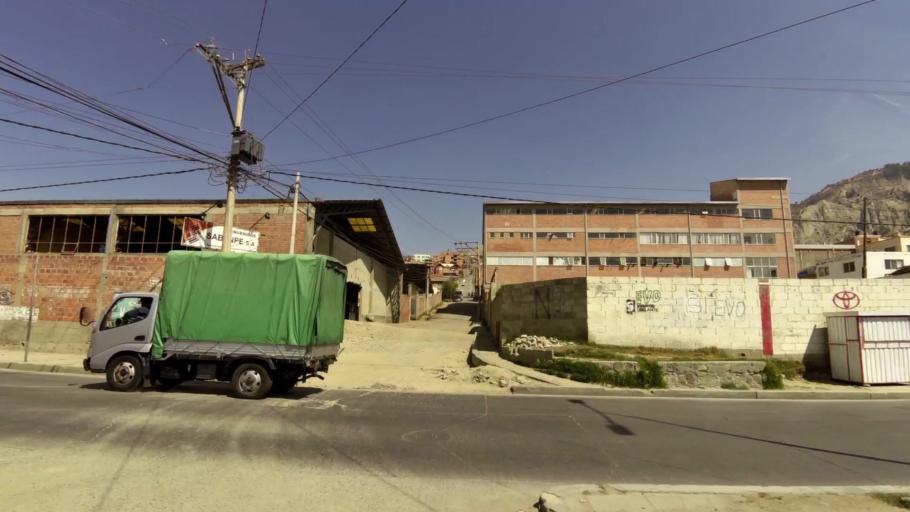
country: BO
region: La Paz
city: La Paz
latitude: -16.5268
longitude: -68.1262
